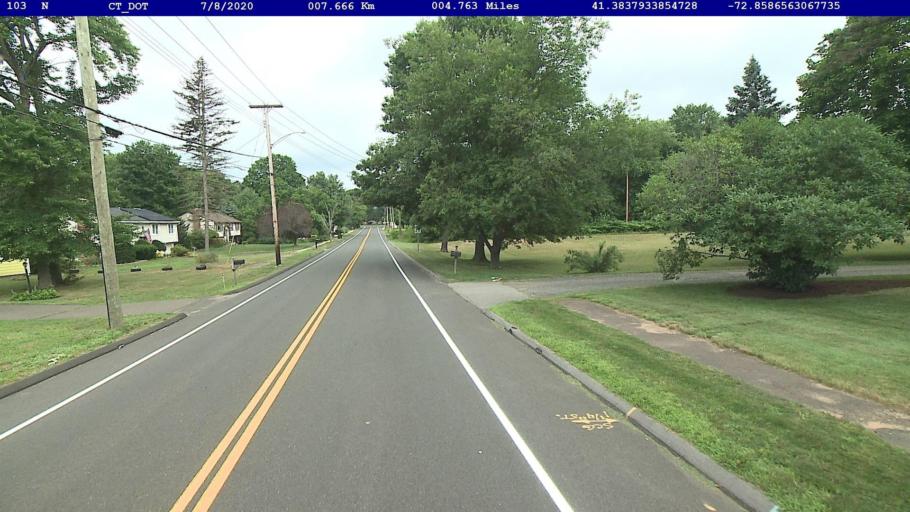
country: US
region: Connecticut
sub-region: New Haven County
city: North Haven
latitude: 41.3838
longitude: -72.8587
